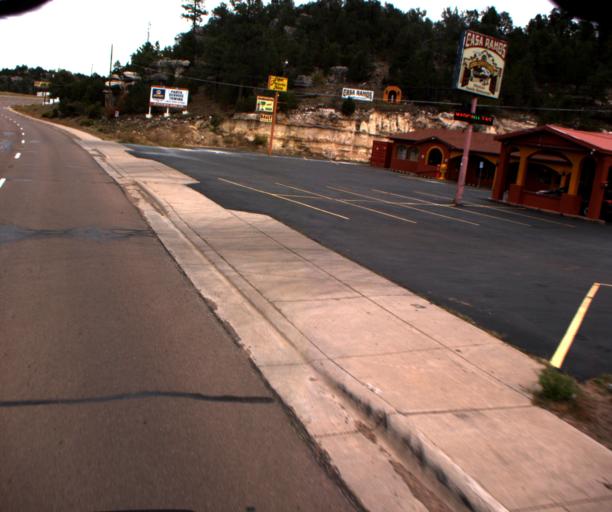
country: US
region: Arizona
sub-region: Navajo County
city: Heber-Overgaard
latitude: 34.4312
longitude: -110.5929
